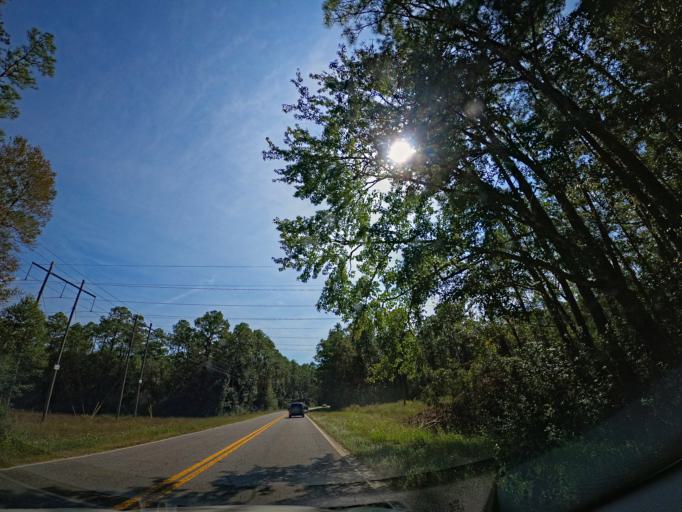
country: US
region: Florida
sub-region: Okaloosa County
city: Crestview
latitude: 30.7451
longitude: -86.6211
